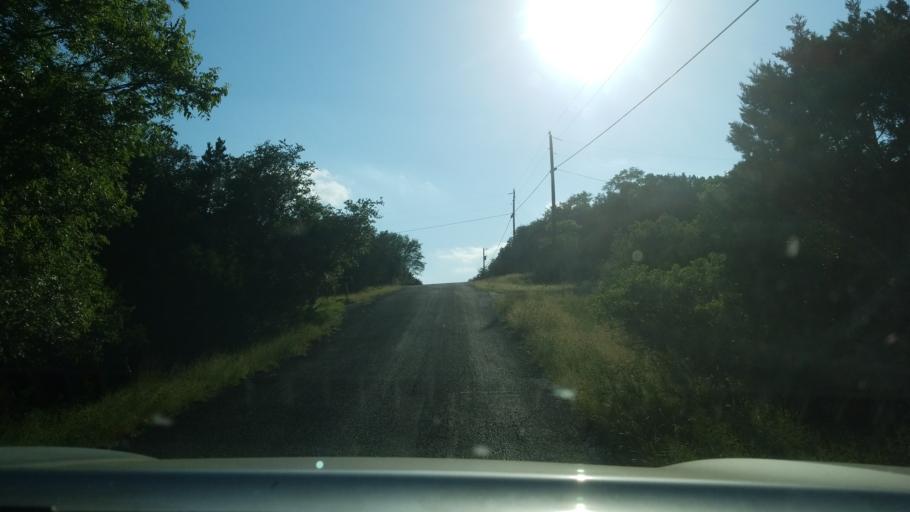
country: US
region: Texas
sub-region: Comal County
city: Bulverde
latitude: 29.7828
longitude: -98.4490
